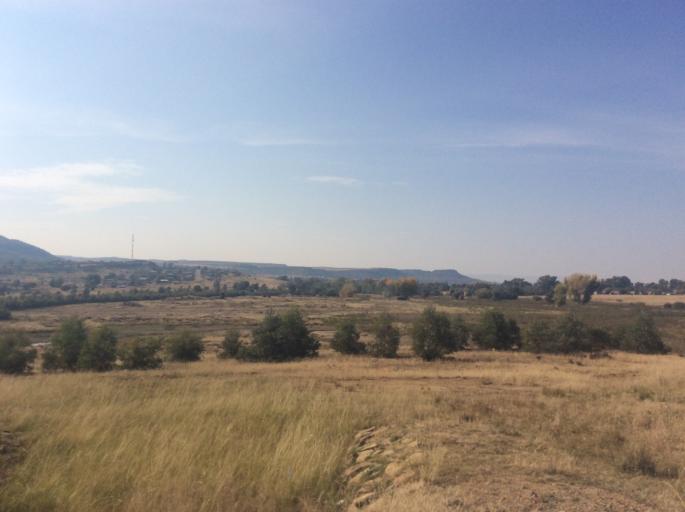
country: LS
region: Mafeteng
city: Mafeteng
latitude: -29.7229
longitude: 27.0178
